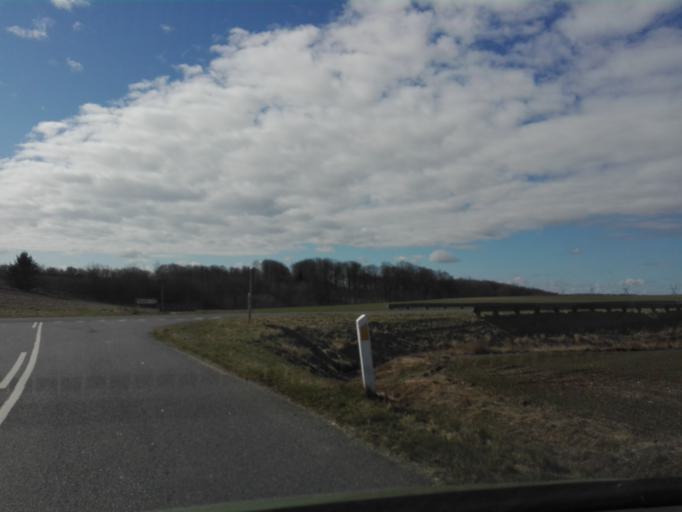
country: DK
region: Central Jutland
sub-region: Horsens Kommune
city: Horsens
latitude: 55.9165
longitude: 9.9212
